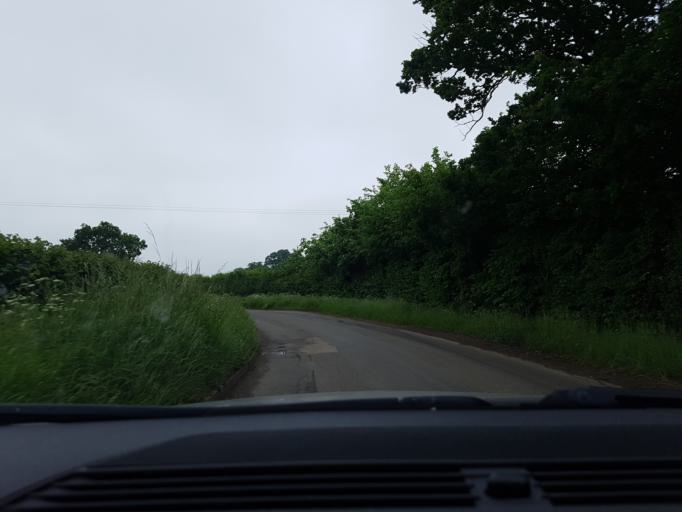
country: GB
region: England
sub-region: Buckinghamshire
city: Steeple Claydon
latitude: 51.9287
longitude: -0.9499
